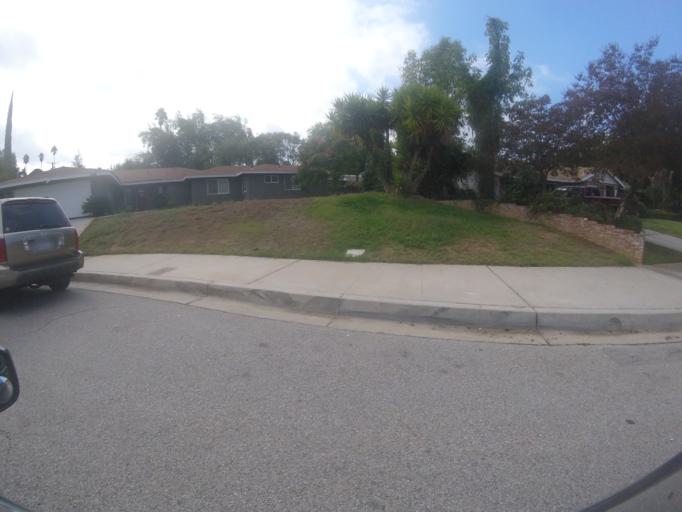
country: US
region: California
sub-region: San Bernardino County
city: Redlands
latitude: 34.0334
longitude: -117.1887
